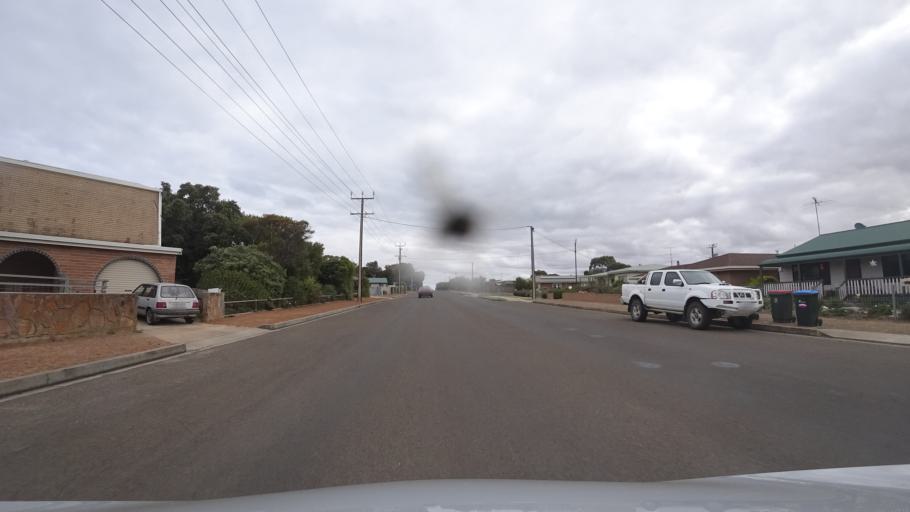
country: AU
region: South Australia
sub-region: Kangaroo Island
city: Kingscote
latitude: -35.6547
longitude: 137.6341
